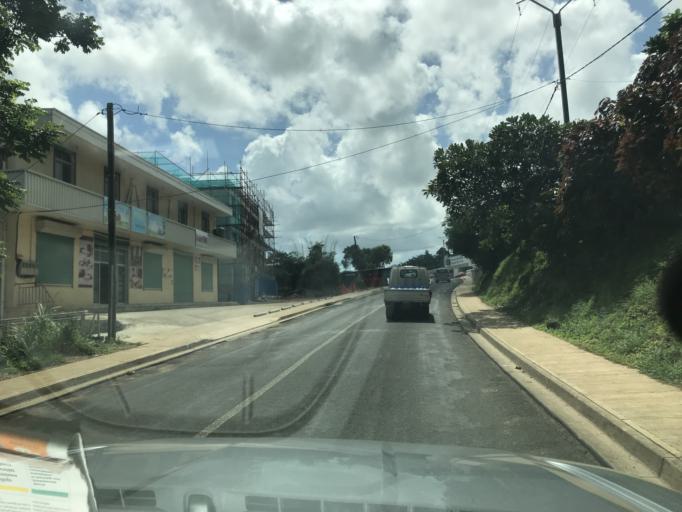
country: VU
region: Shefa
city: Port-Vila
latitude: -17.7243
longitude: 168.3109
